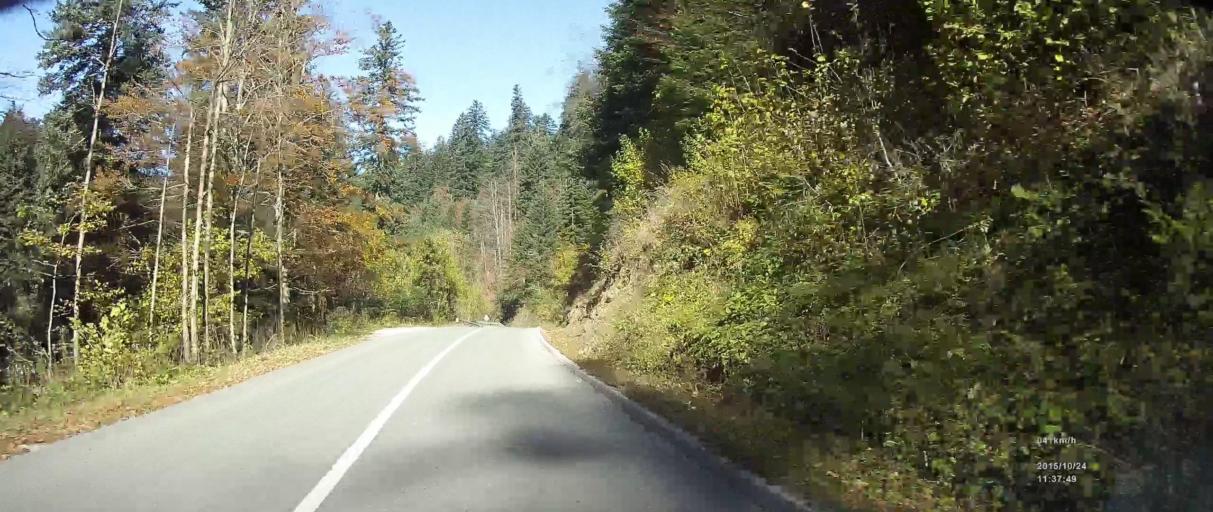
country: HR
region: Primorsko-Goranska
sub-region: Grad Delnice
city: Delnice
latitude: 45.4003
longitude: 14.7031
